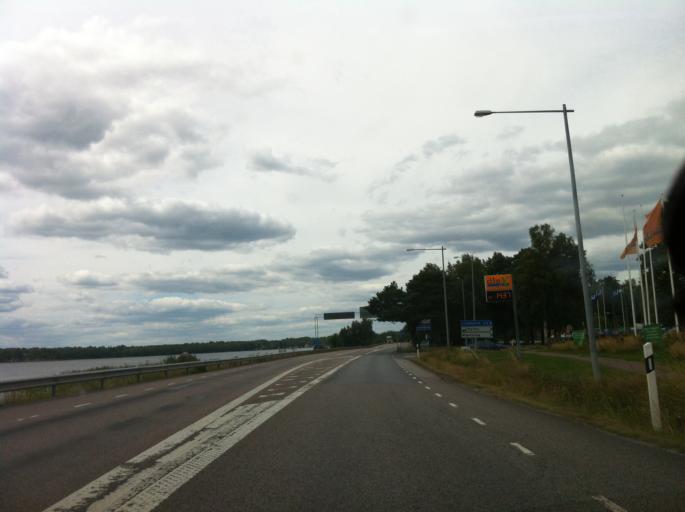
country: SE
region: Kronoberg
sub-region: Tingsryds Kommun
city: Tingsryd
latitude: 56.5176
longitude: 14.9869
